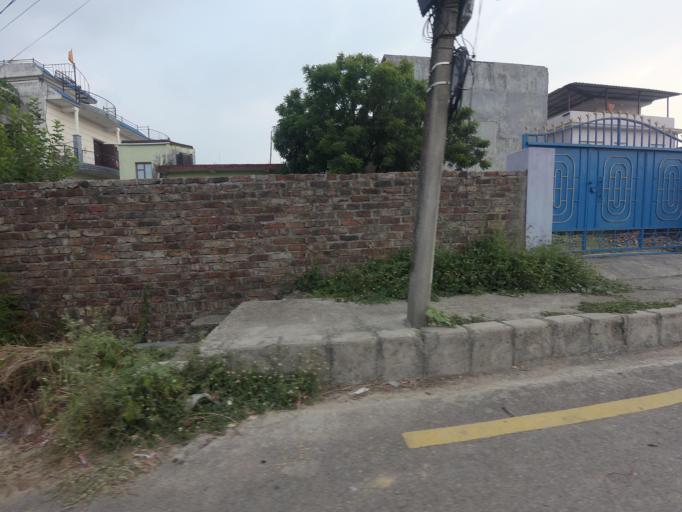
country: NP
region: Western Region
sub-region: Lumbini Zone
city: Bhairahawa
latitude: 27.4979
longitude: 83.4456
